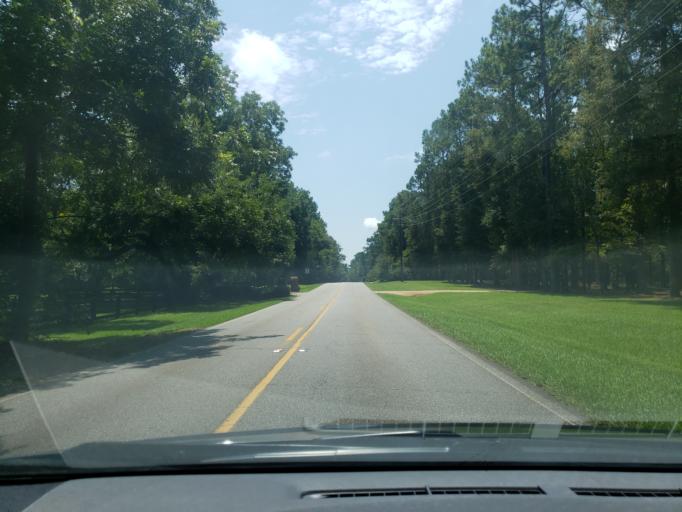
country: US
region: Georgia
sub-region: Dougherty County
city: Albany
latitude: 31.5995
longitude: -84.2779
